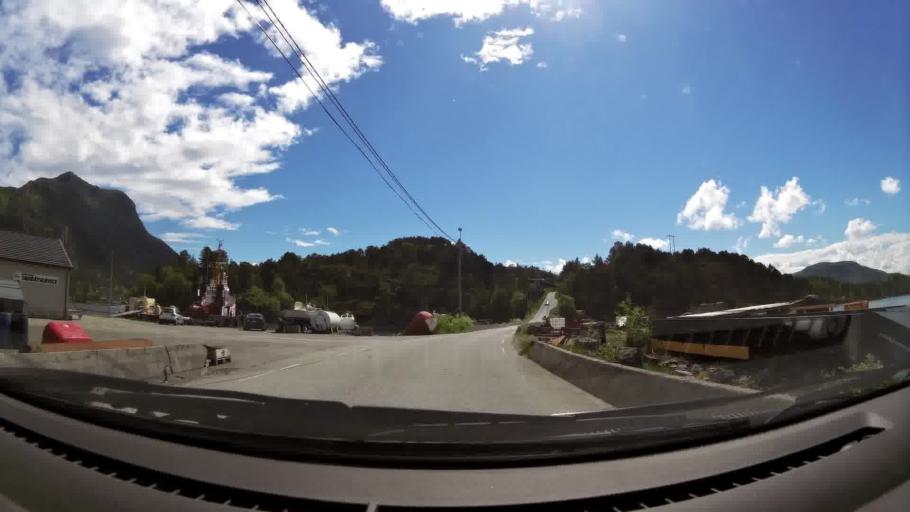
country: NO
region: More og Romsdal
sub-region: Kristiansund
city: Kristiansund
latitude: 63.0580
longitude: 7.7127
